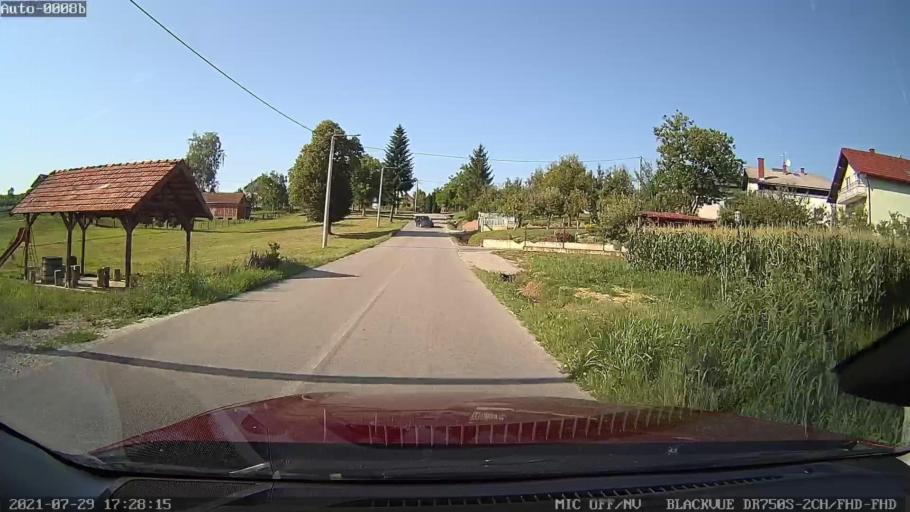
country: HR
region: Varazdinska
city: Ivanec
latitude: 46.2672
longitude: 16.1162
